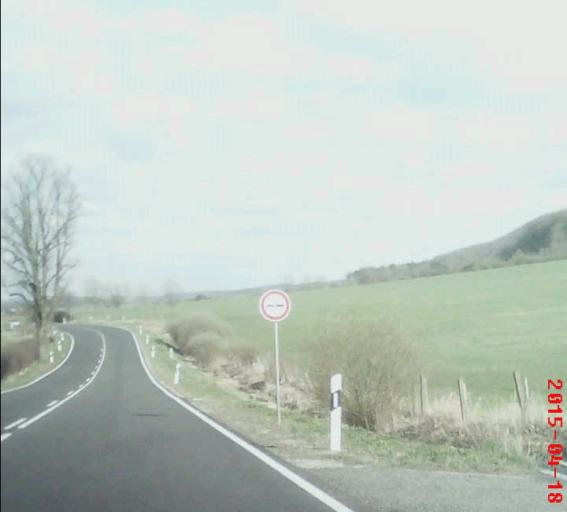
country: DE
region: Thuringia
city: Wingerode
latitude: 51.3802
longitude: 10.2314
